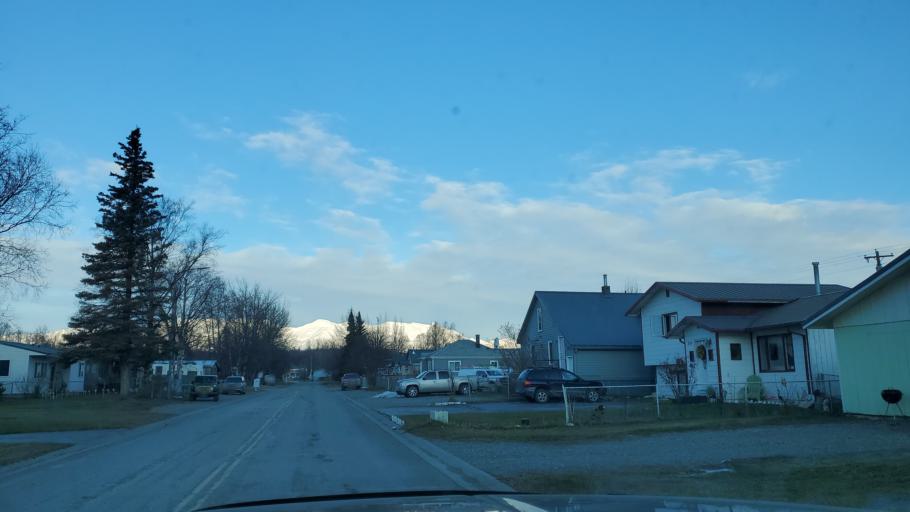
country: US
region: Alaska
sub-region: Matanuska-Susitna Borough
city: Palmer
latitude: 61.6034
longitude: -149.1165
